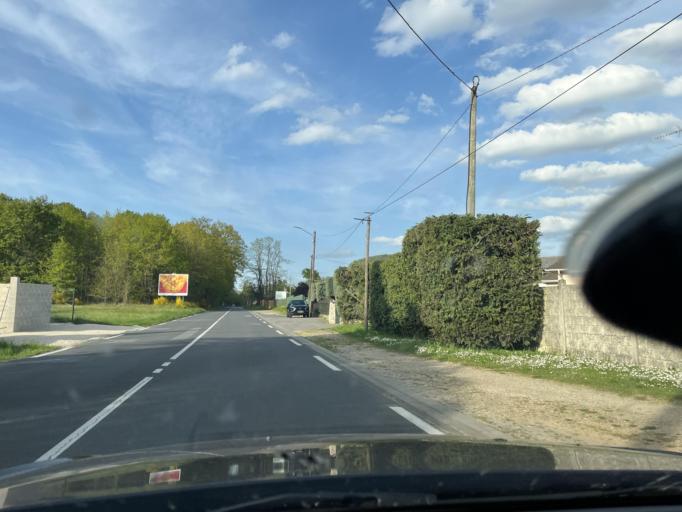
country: FR
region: Ile-de-France
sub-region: Departement de l'Essonne
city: Breuillet
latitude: 48.5604
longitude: 2.1531
